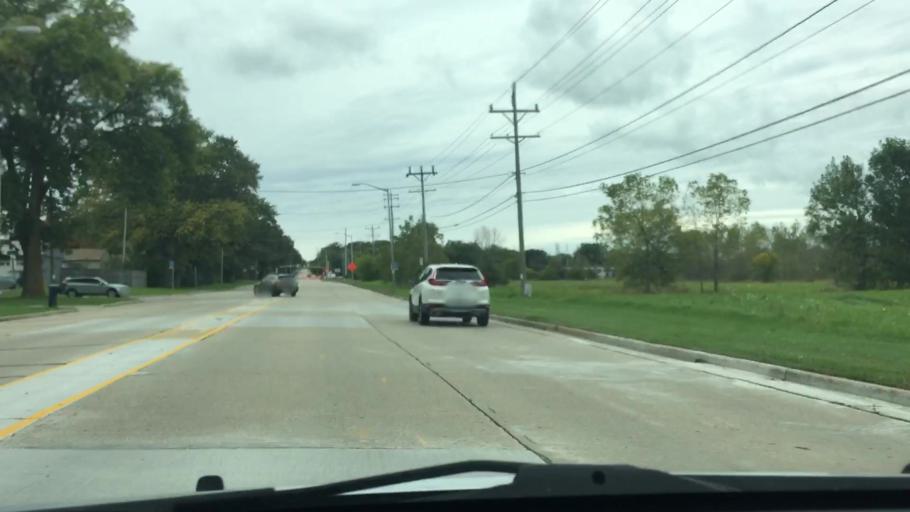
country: US
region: Wisconsin
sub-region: Waukesha County
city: Waukesha
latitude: 43.0323
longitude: -88.2504
